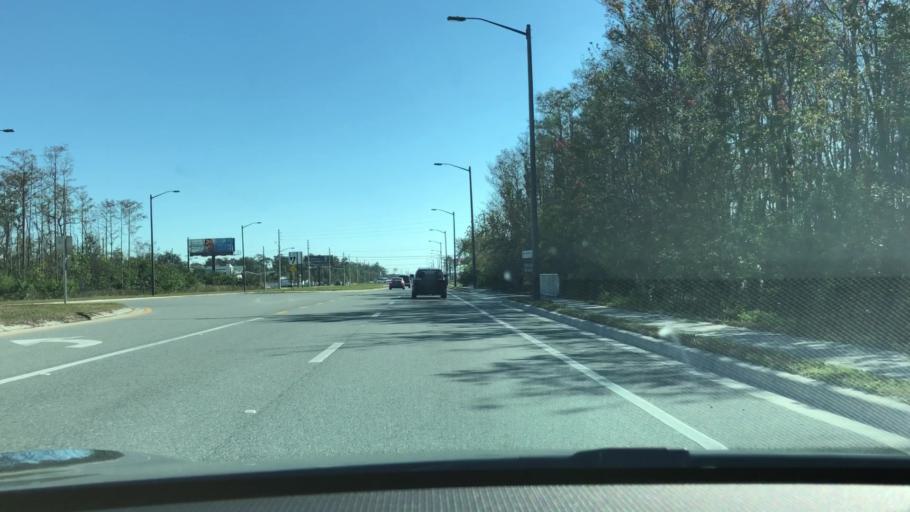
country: US
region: Florida
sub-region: Orange County
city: Conway
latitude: 28.4588
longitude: -81.2712
